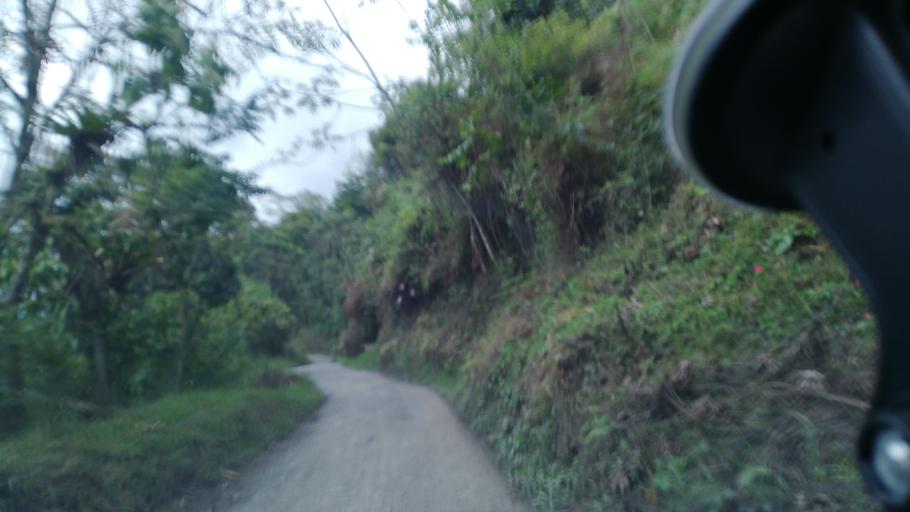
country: CO
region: Cundinamarca
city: Pacho
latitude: 5.1560
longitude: -74.2471
